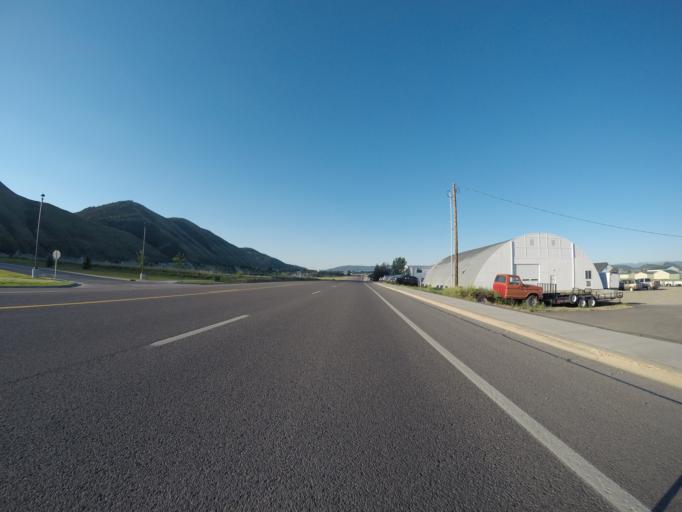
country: US
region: Wyoming
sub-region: Lincoln County
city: Afton
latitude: 42.7114
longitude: -110.9336
